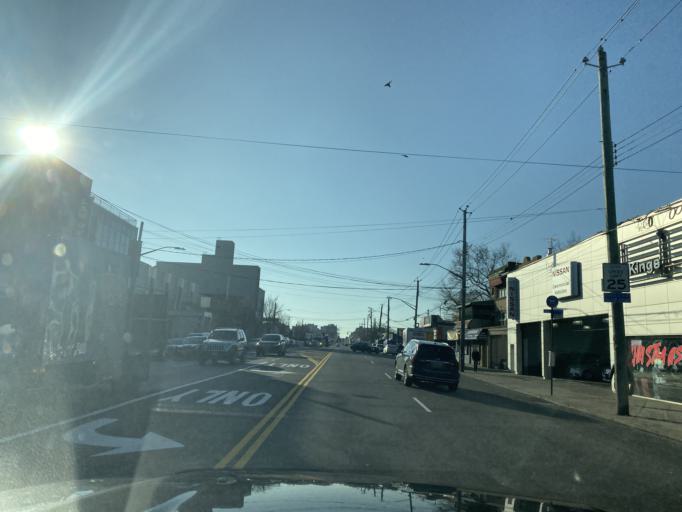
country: US
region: New York
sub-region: Kings County
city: Coney Island
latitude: 40.5894
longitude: -73.9605
